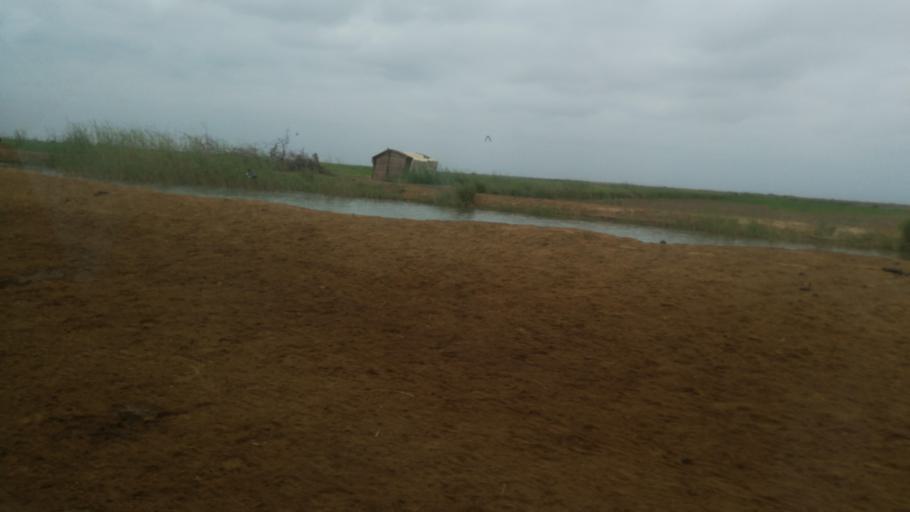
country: SN
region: Saint-Louis
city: Saint-Louis
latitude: 16.3157
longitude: -16.2317
